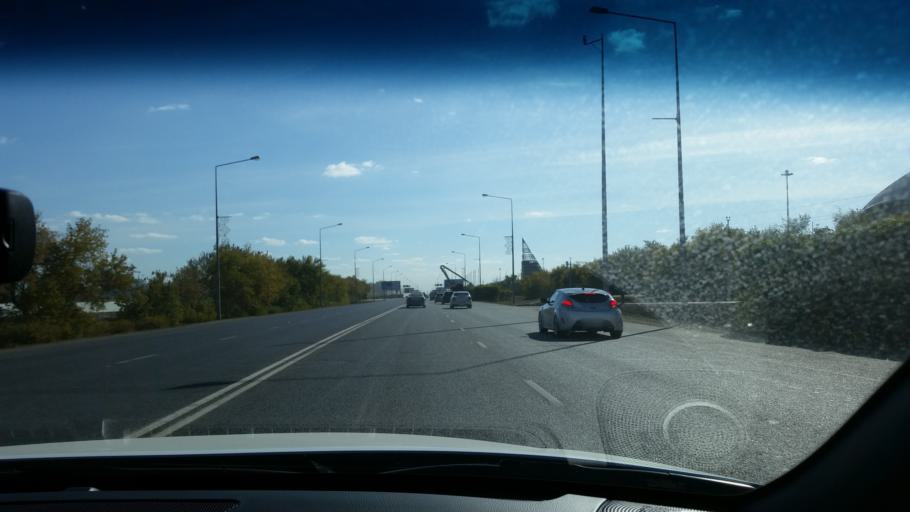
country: KZ
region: Astana Qalasy
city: Astana
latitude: 51.1111
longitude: 71.4104
